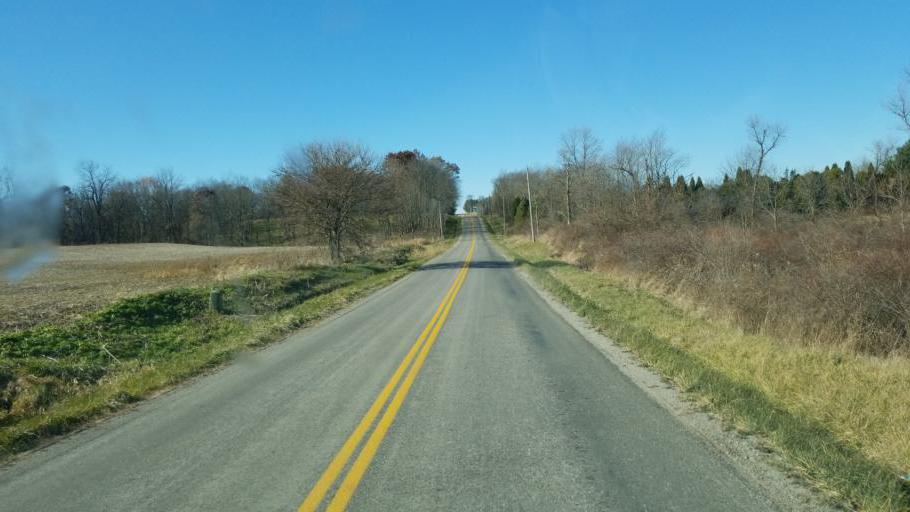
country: US
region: Ohio
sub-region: Ashland County
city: Ashland
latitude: 40.9534
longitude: -82.3768
